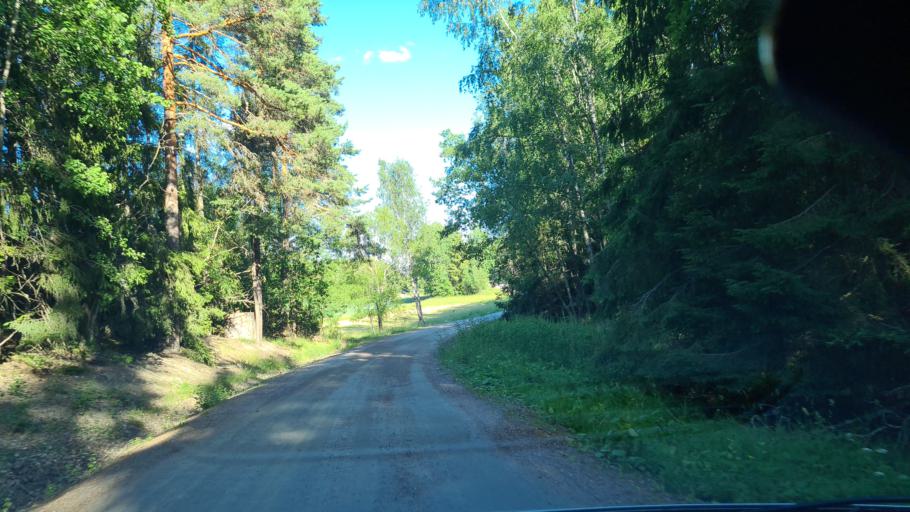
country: SE
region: Soedermanland
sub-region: Nykopings Kommun
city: Nykoping
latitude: 58.9209
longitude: 17.0332
